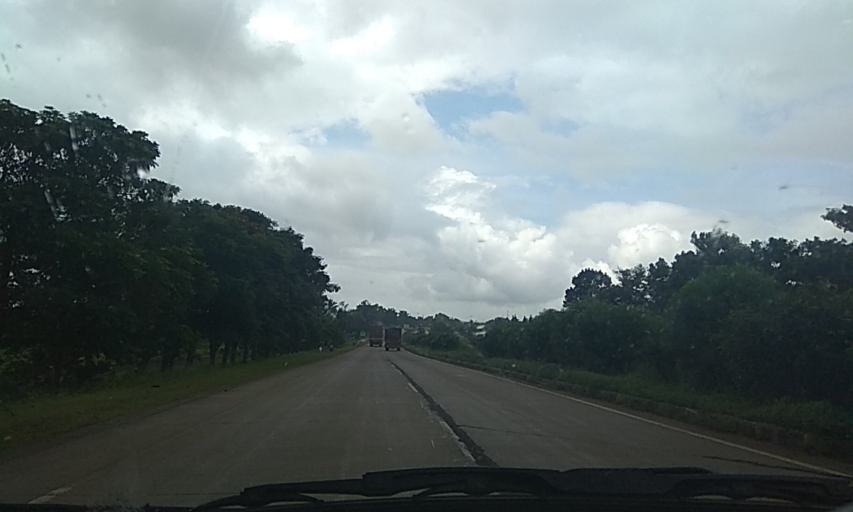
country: IN
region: Karnataka
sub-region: Belgaum
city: Sankeshwar
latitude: 16.2932
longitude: 74.4391
